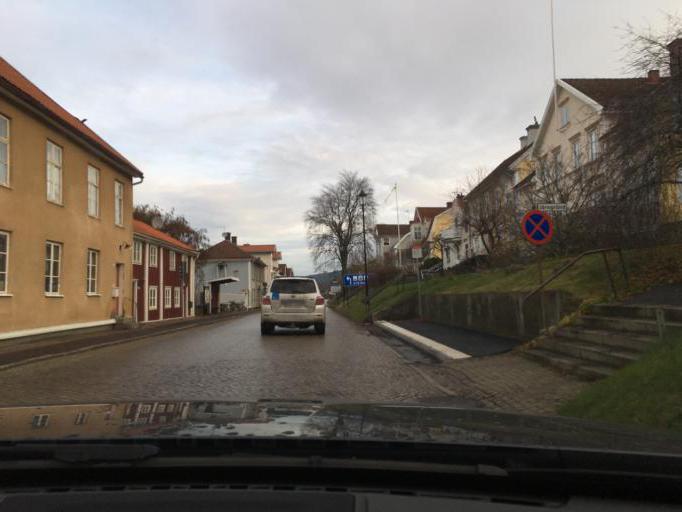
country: SE
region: Joenkoeping
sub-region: Jonkopings Kommun
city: Graenna
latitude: 58.0244
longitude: 14.4693
